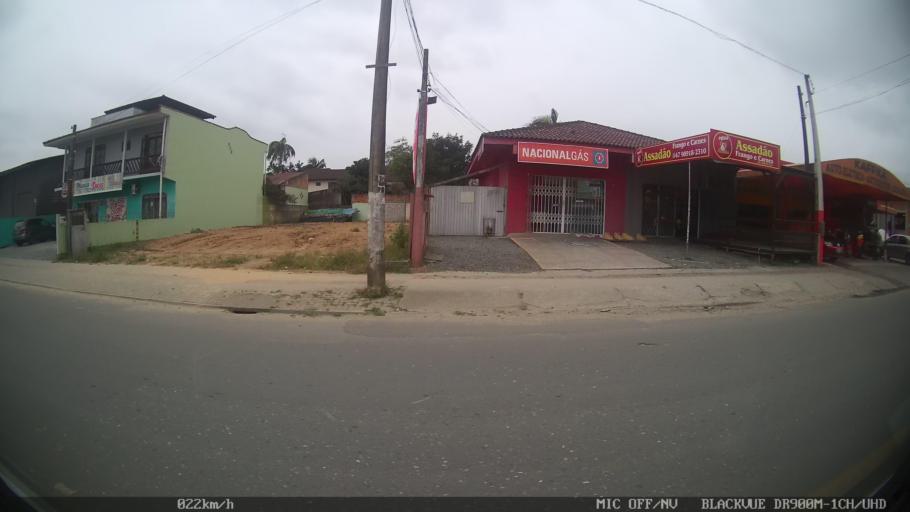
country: BR
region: Santa Catarina
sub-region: Joinville
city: Joinville
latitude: -26.3646
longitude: -48.8294
